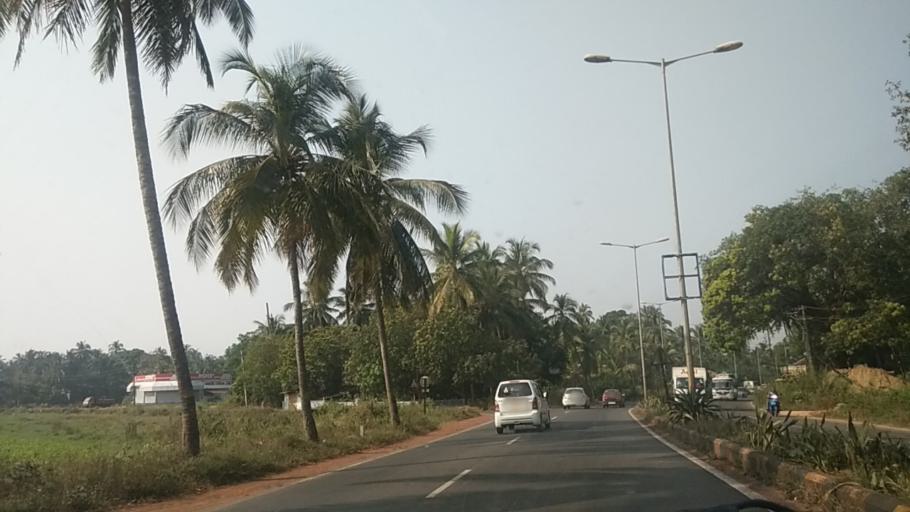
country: IN
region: Goa
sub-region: North Goa
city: Guirim
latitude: 15.5662
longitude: 73.8079
